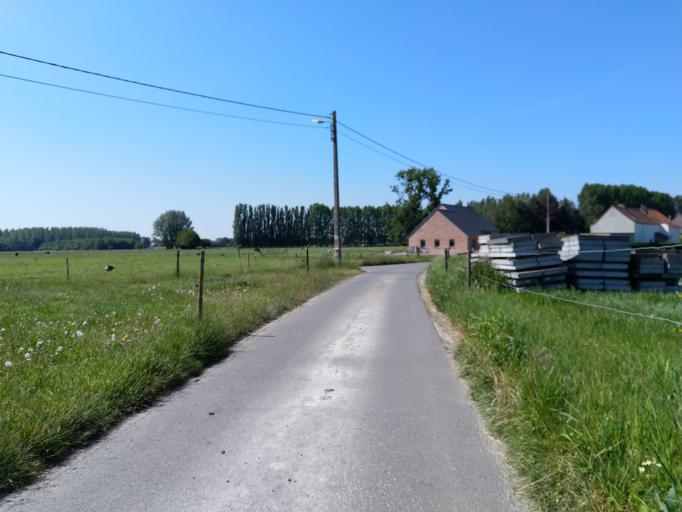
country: BE
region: Wallonia
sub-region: Province du Hainaut
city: Lens
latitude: 50.5466
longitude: 3.8714
